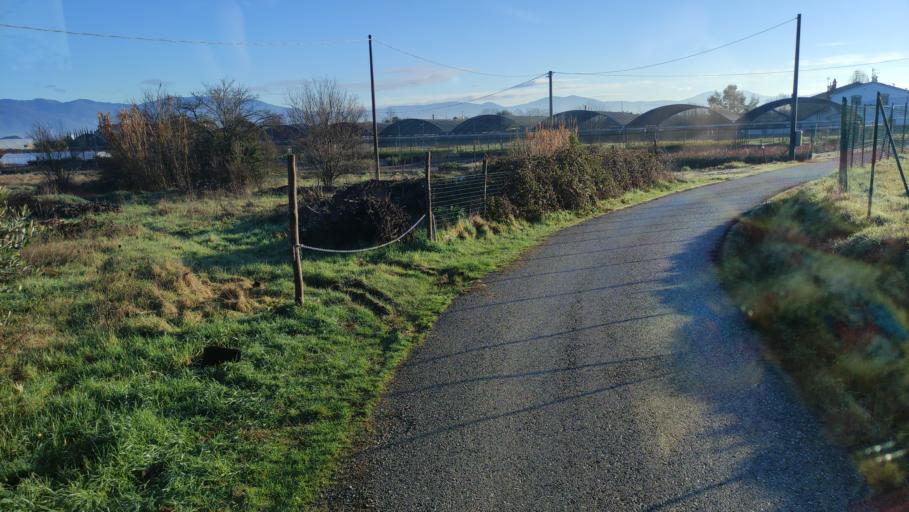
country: IT
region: Tuscany
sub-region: Provincia di Pistoia
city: Cantagrillo-Casalguidi
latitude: 43.8719
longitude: 10.9349
